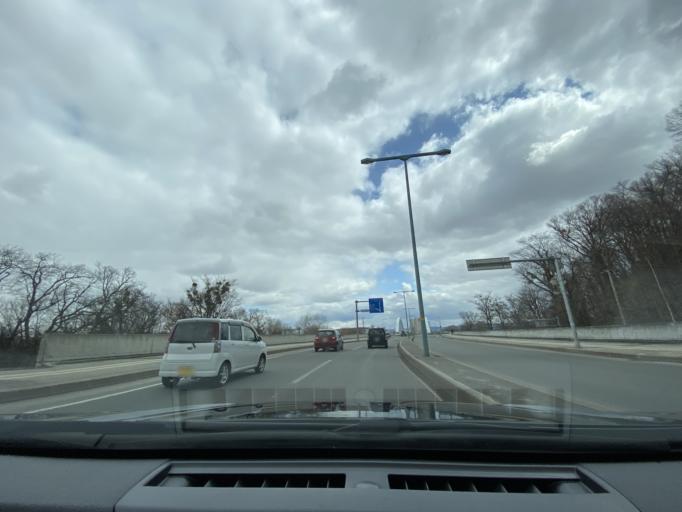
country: JP
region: Hokkaido
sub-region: Asahikawa-shi
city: Asahikawa
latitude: 43.7541
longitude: 142.3632
